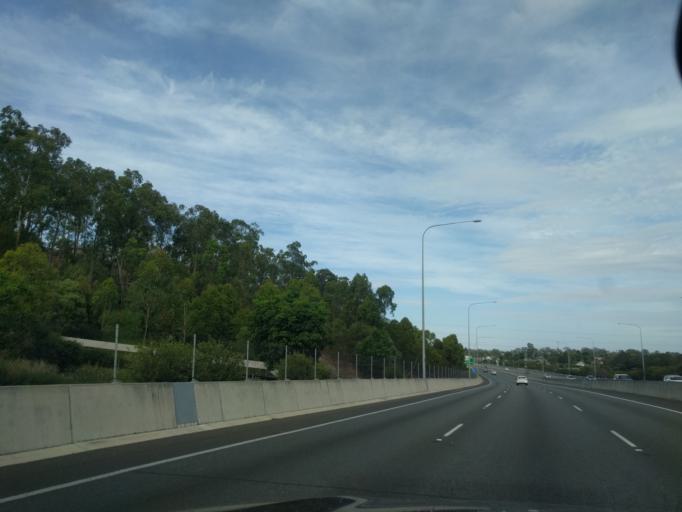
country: AU
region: Queensland
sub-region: Ipswich
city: Redbank
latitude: -27.6013
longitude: 152.8832
